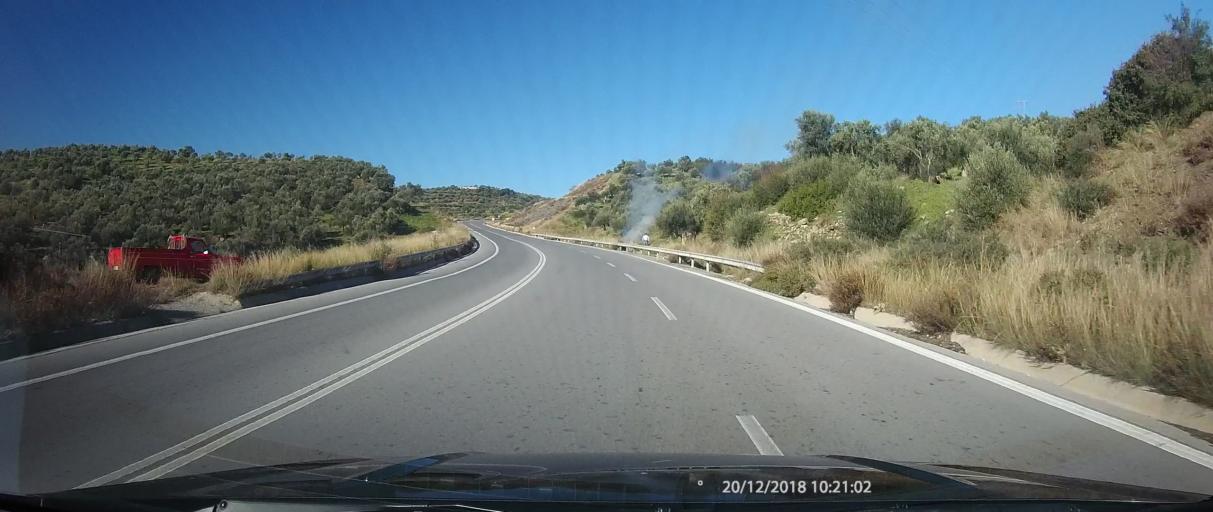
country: GR
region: Peloponnese
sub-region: Nomos Lakonias
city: Magoula
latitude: 37.1560
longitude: 22.4310
